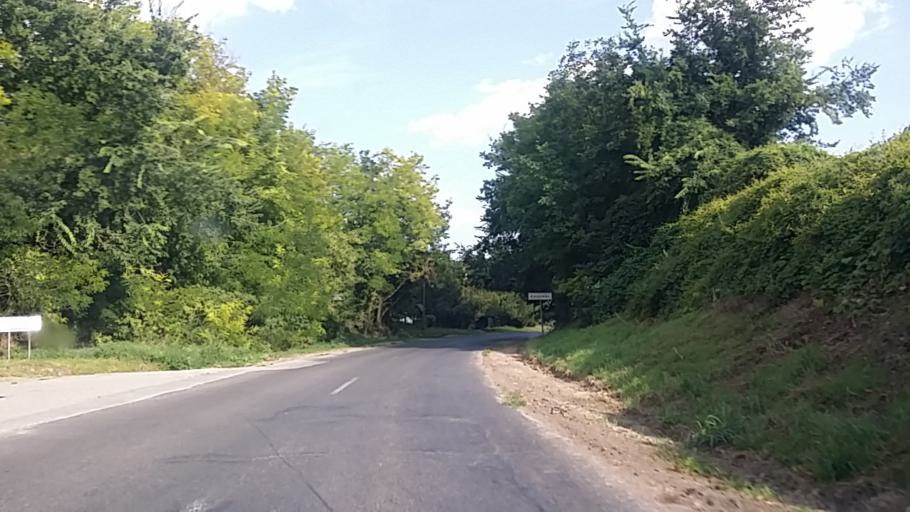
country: HU
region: Tolna
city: Gyonk
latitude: 46.5078
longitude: 18.5573
